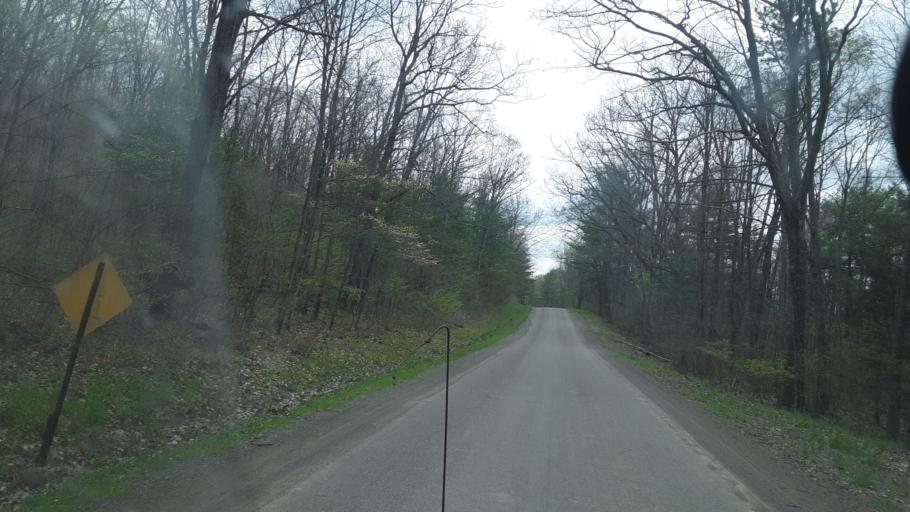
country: US
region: New York
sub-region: Steuben County
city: Addison
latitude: 42.0960
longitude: -77.3147
